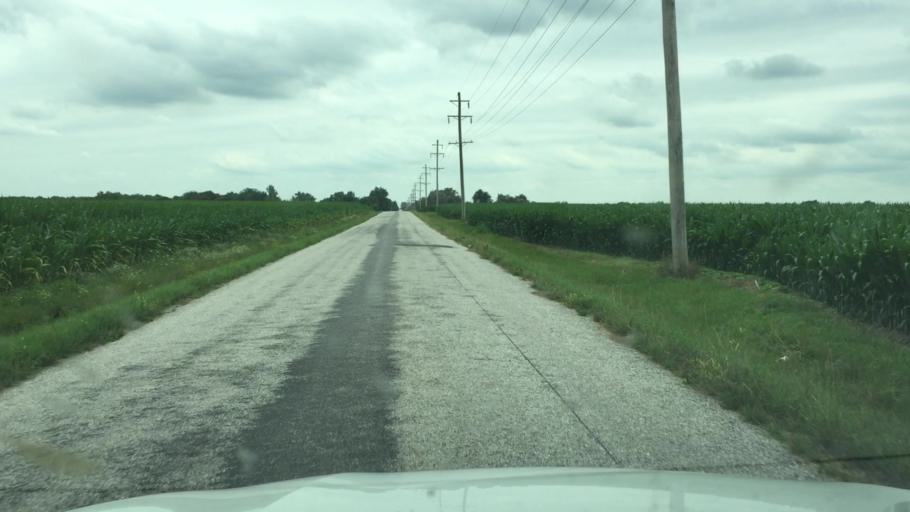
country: US
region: Illinois
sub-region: Hancock County
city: Carthage
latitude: 40.3369
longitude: -91.0824
